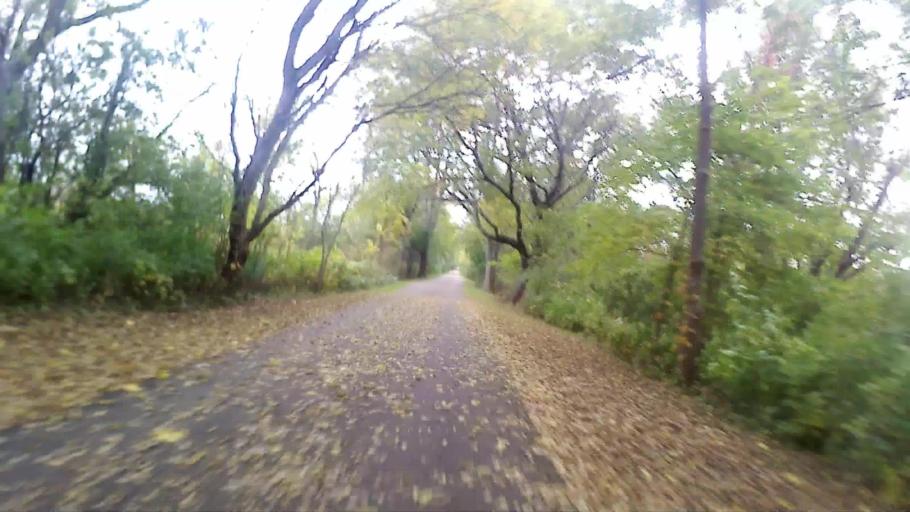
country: US
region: Illinois
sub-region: Kane County
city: Sugar Grove
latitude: 41.7703
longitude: -88.4047
